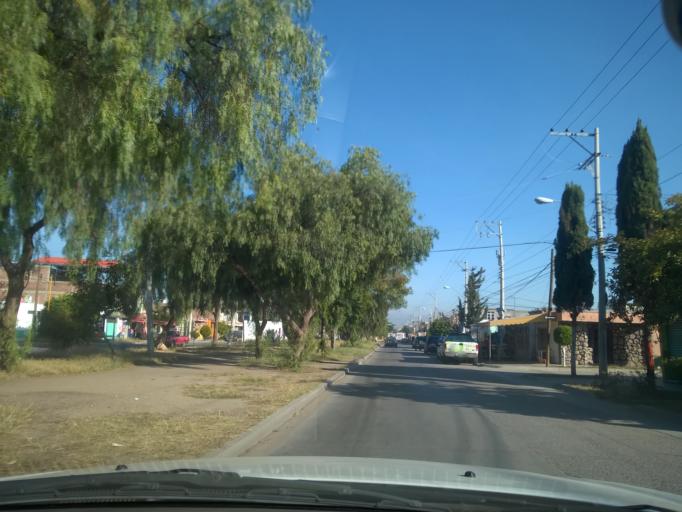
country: MX
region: Guanajuato
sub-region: Leon
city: San Jose de Duran (Los Troncoso)
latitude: 21.0776
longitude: -101.6446
